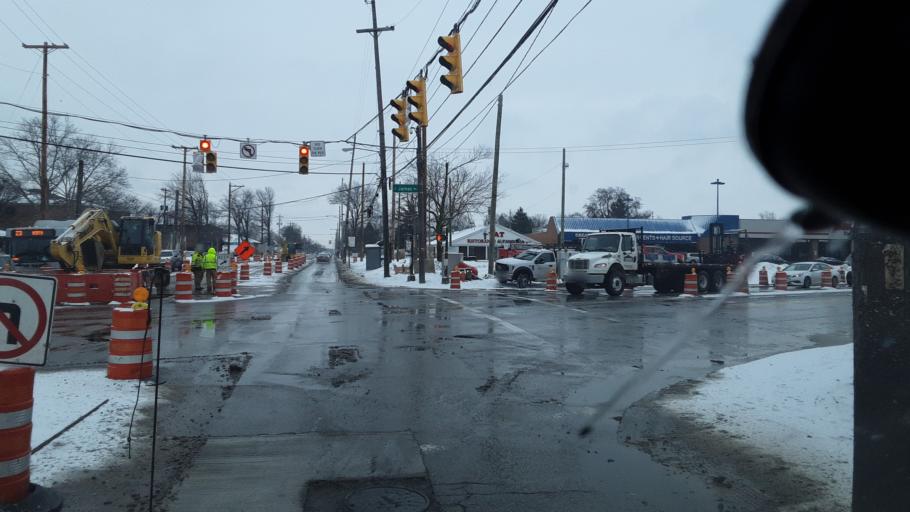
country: US
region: Ohio
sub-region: Franklin County
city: Bexley
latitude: 39.9468
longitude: -82.9158
